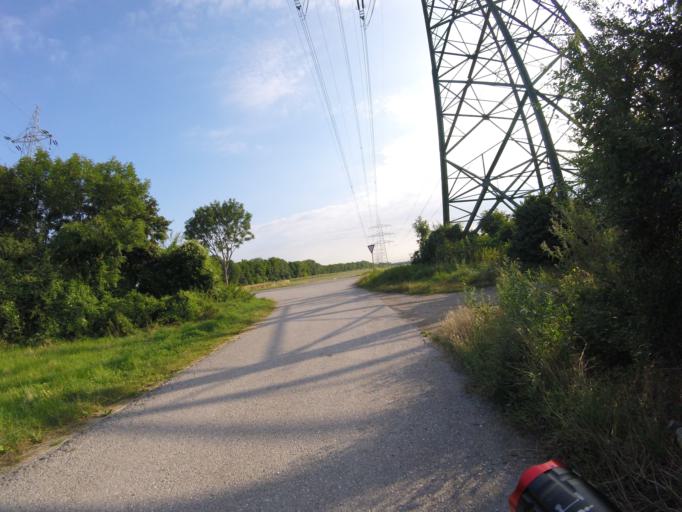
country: AT
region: Lower Austria
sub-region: Politischer Bezirk Baden
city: Trumau
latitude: 47.9988
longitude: 16.3730
